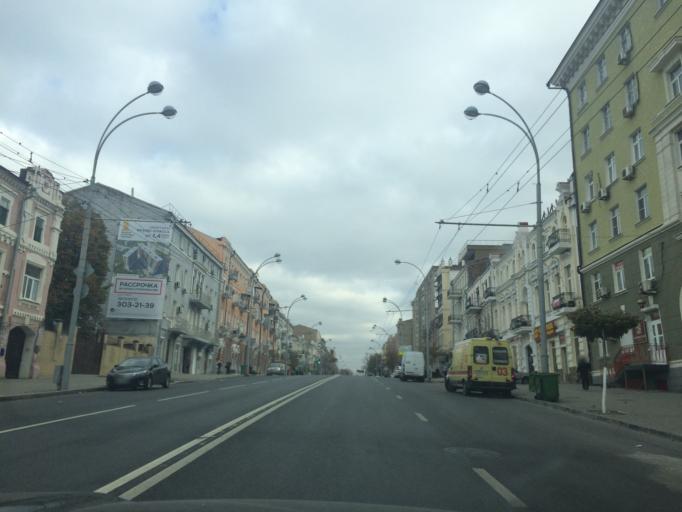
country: RU
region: Rostov
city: Rostov-na-Donu
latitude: 47.2181
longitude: 39.6982
